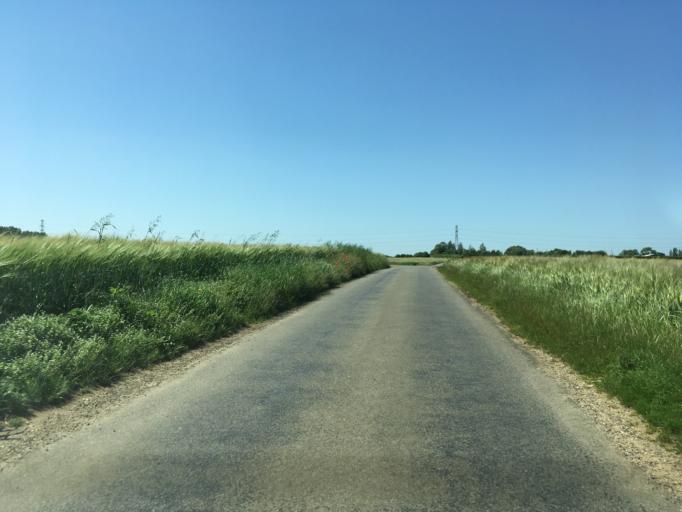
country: GB
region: England
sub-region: Northamptonshire
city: Brackley
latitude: 52.0030
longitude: -1.0948
